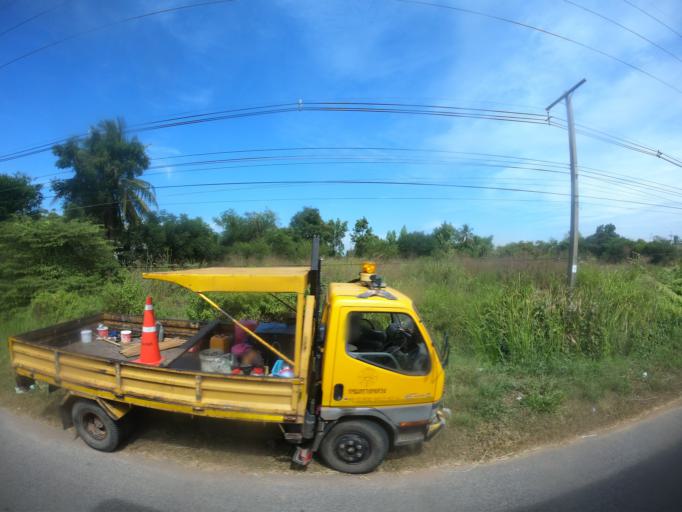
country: TH
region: Maha Sarakham
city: Chiang Yuen
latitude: 16.4430
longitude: 102.9910
